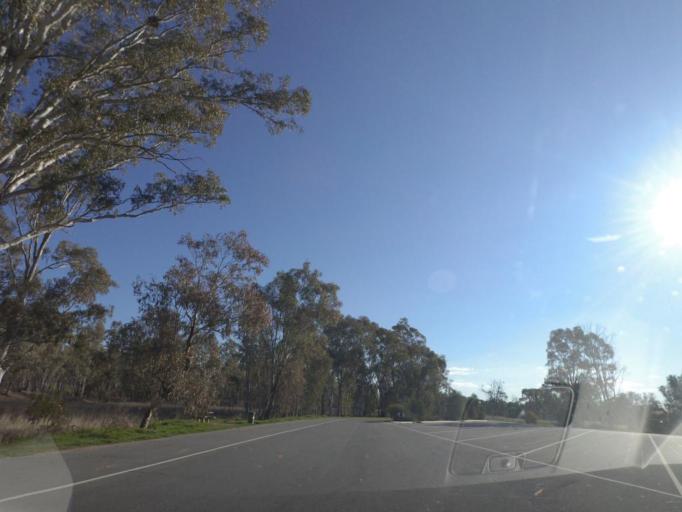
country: AU
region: Victoria
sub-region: Benalla
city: Benalla
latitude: -36.5775
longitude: 145.9206
